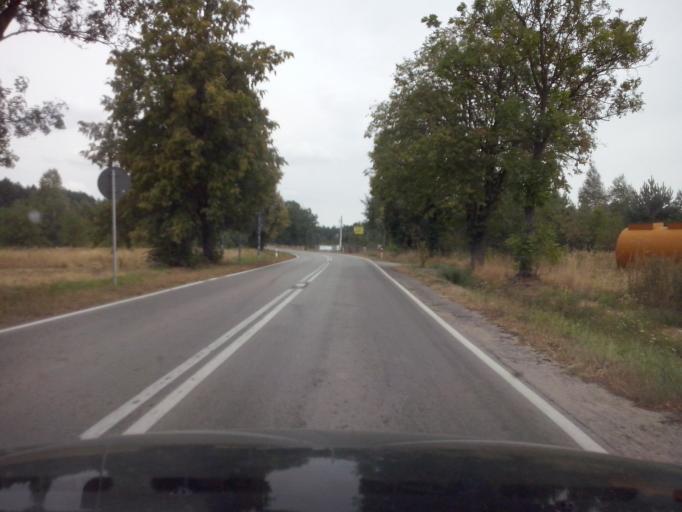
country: PL
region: Swietokrzyskie
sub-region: Powiat kielecki
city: Rakow
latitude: 50.6827
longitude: 21.0536
